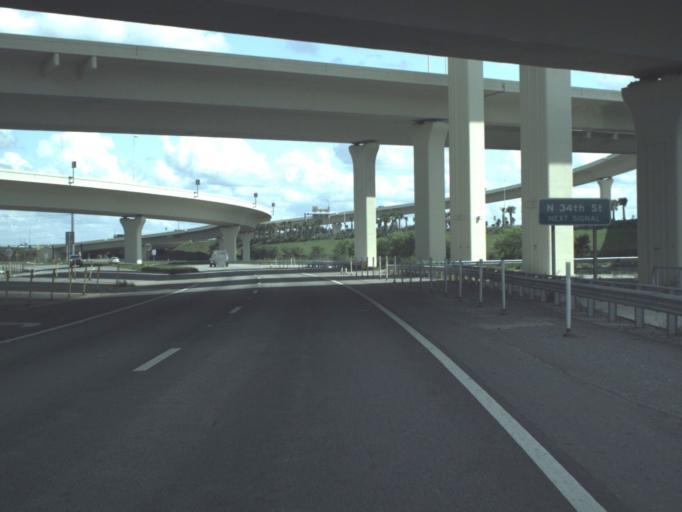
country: US
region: Florida
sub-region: Hillsborough County
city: Tampa
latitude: 27.9548
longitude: -82.4264
